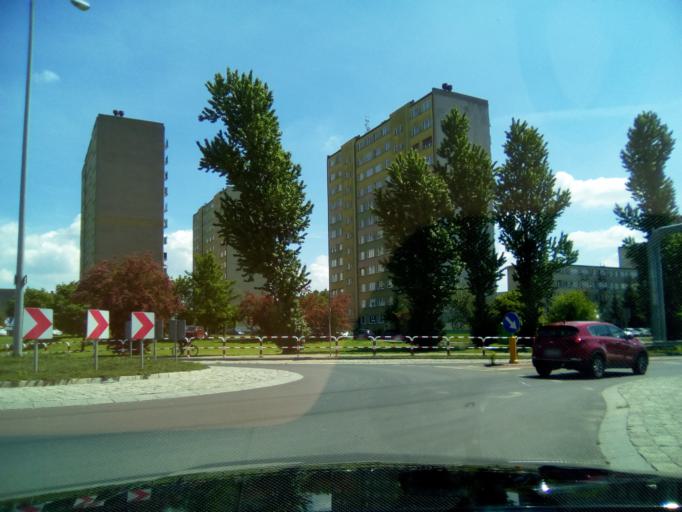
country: PL
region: Greater Poland Voivodeship
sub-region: Powiat gnieznienski
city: Gniezno
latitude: 52.5528
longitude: 17.6047
